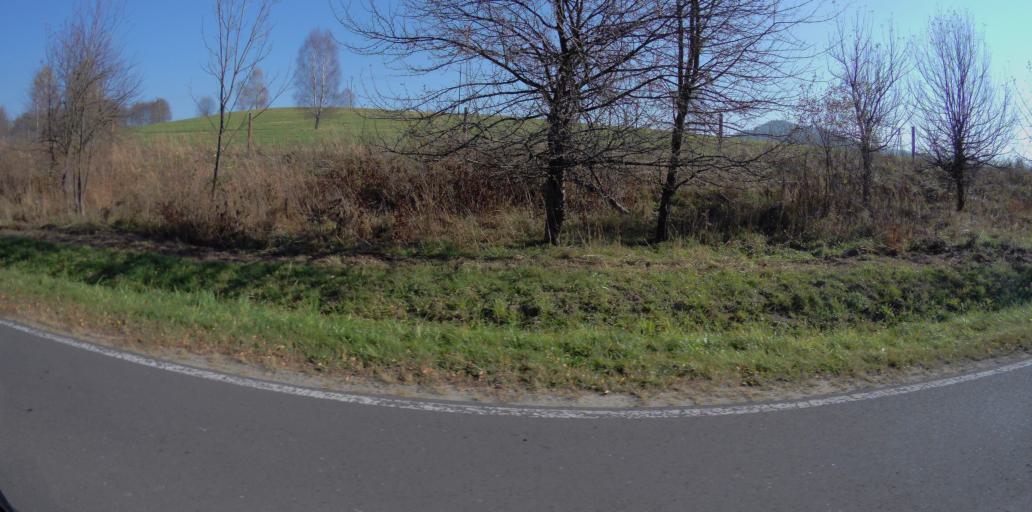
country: PL
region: Subcarpathian Voivodeship
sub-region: Powiat bieszczadzki
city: Lutowiska
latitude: 49.2052
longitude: 22.6762
